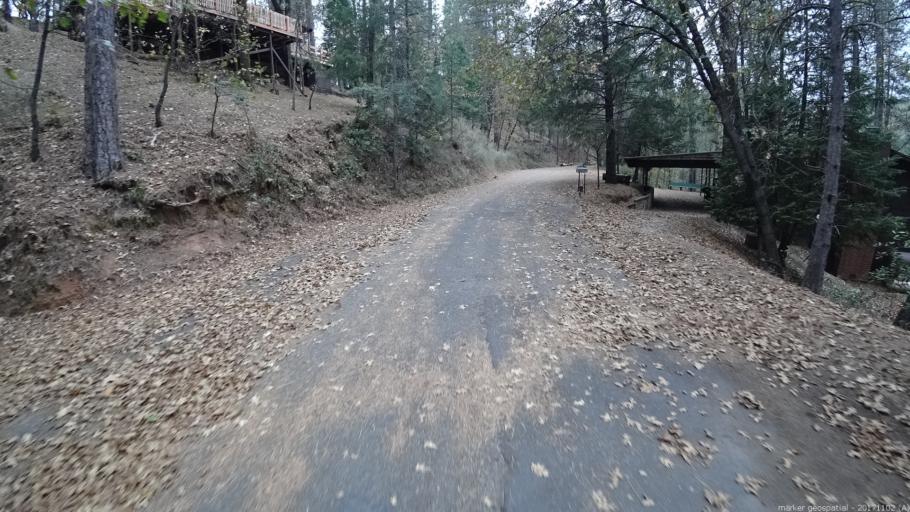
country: US
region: California
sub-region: Shasta County
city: Bella Vista
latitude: 40.7474
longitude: -122.2380
